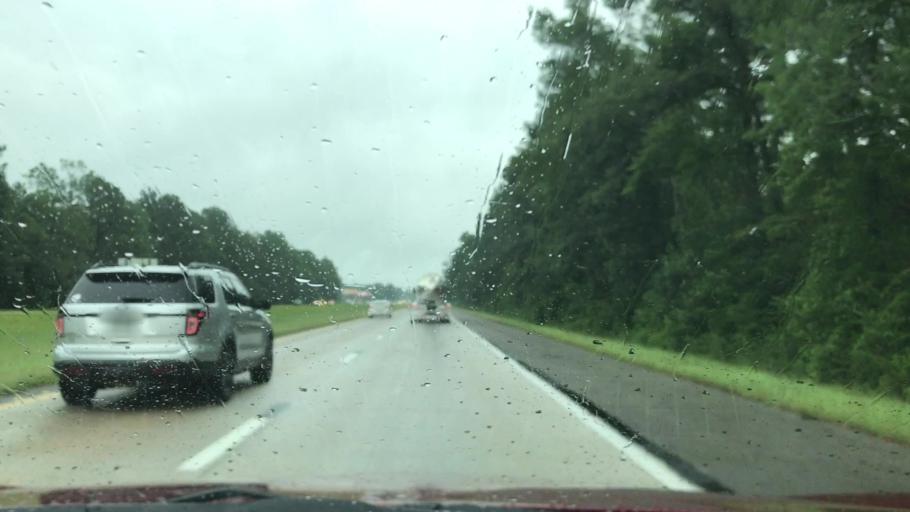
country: US
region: South Carolina
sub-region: Orangeburg County
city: Holly Hill
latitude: 33.2514
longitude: -80.4697
